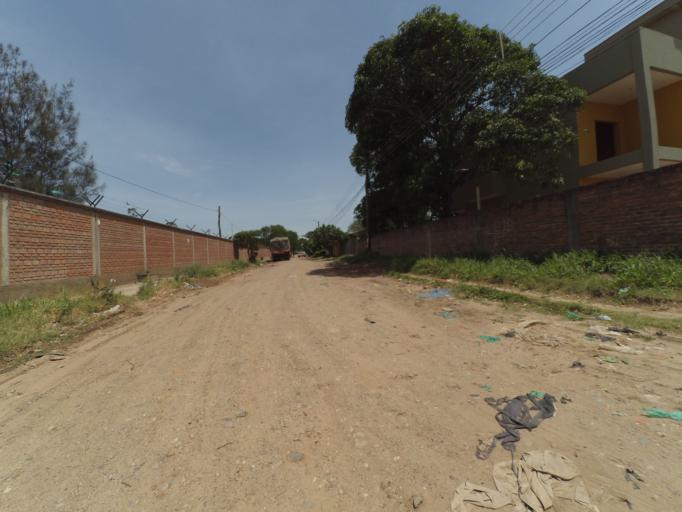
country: BO
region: Santa Cruz
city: Santa Cruz de la Sierra
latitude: -17.8316
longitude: -63.2375
